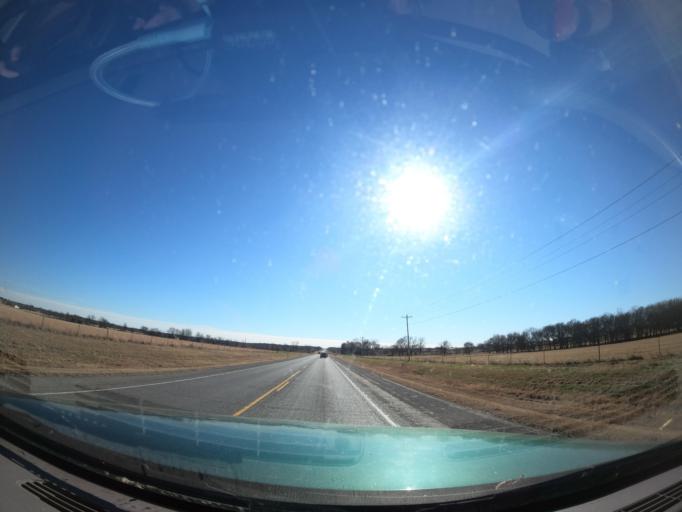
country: US
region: Oklahoma
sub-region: Muskogee County
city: Haskell
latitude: 35.8594
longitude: -95.6775
